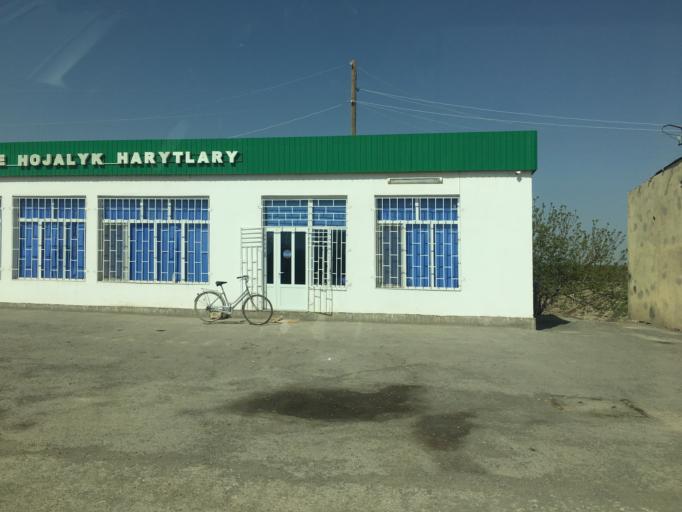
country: TM
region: Lebap
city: Turkmenabat
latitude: 38.9677
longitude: 63.6543
